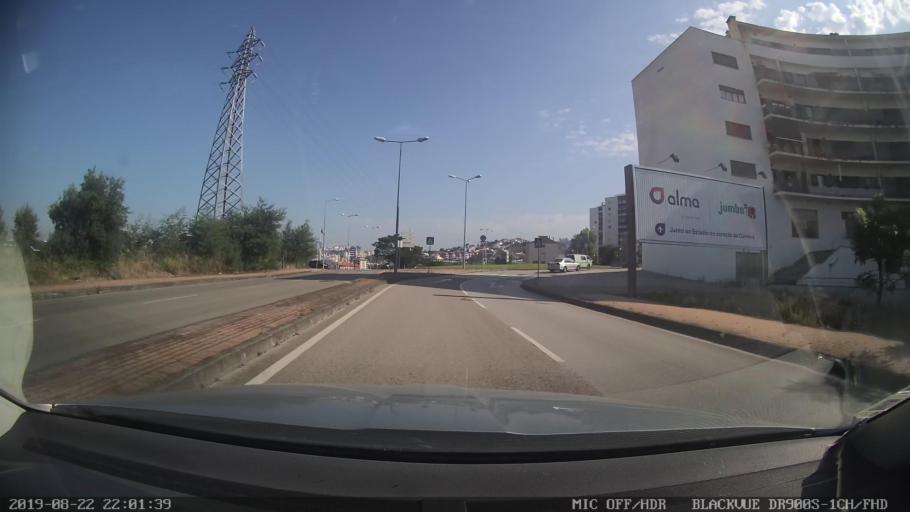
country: PT
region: Coimbra
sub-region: Coimbra
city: Coimbra
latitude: 40.1932
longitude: -8.3988
